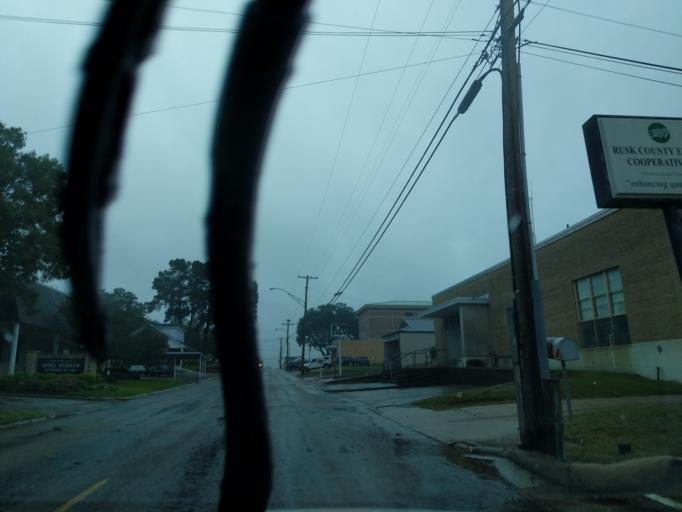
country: US
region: Texas
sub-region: Panola County
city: Carthage
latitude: 32.1559
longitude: -94.3428
